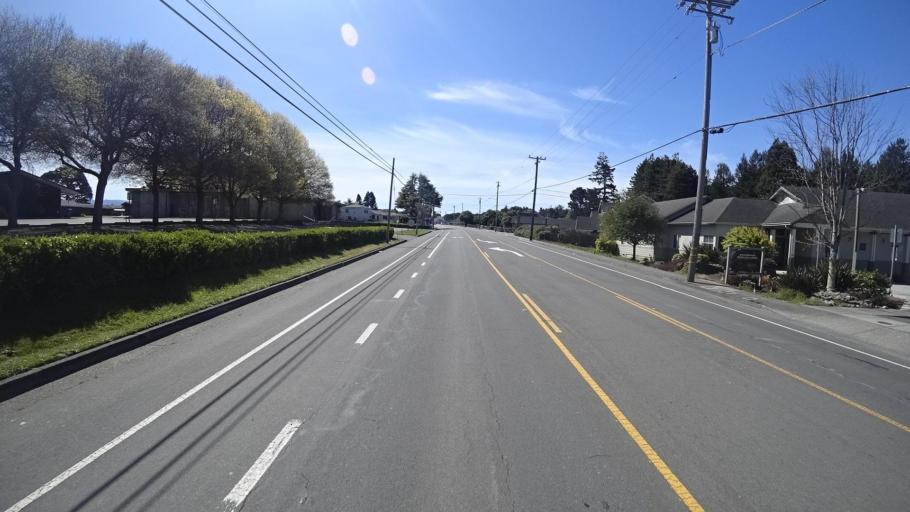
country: US
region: California
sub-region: Humboldt County
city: Myrtletown
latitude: 40.7897
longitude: -124.1335
